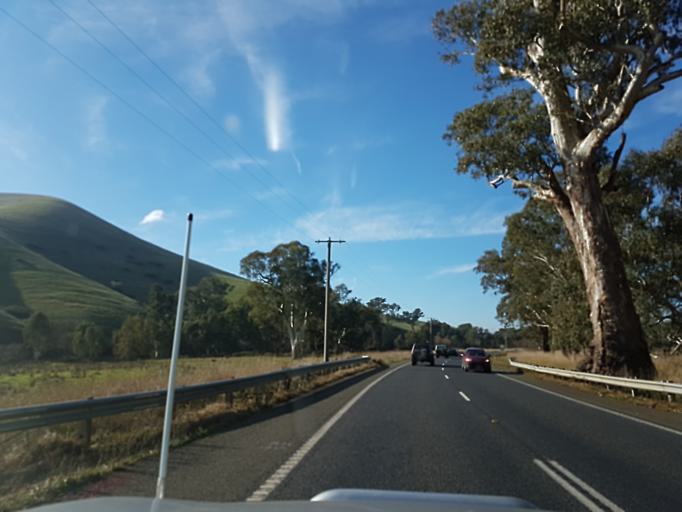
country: AU
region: Victoria
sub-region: Murrindindi
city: Alexandra
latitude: -37.1551
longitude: 145.5675
